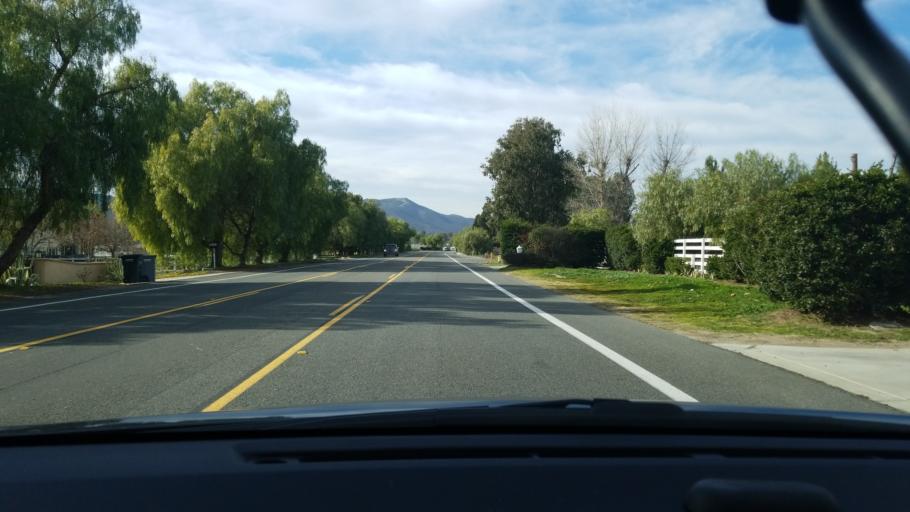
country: US
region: California
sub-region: Riverside County
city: Temecula
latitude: 33.4794
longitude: -117.1278
